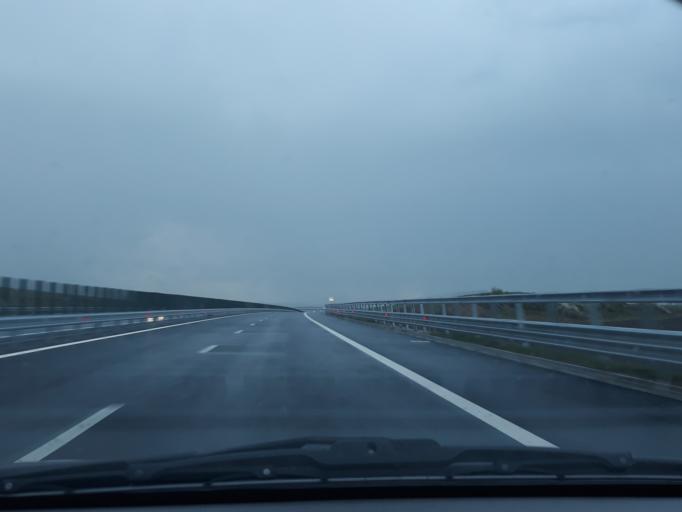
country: RO
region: Mures
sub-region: Comuna Ogra
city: Ogra
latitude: 46.4378
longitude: 24.3308
